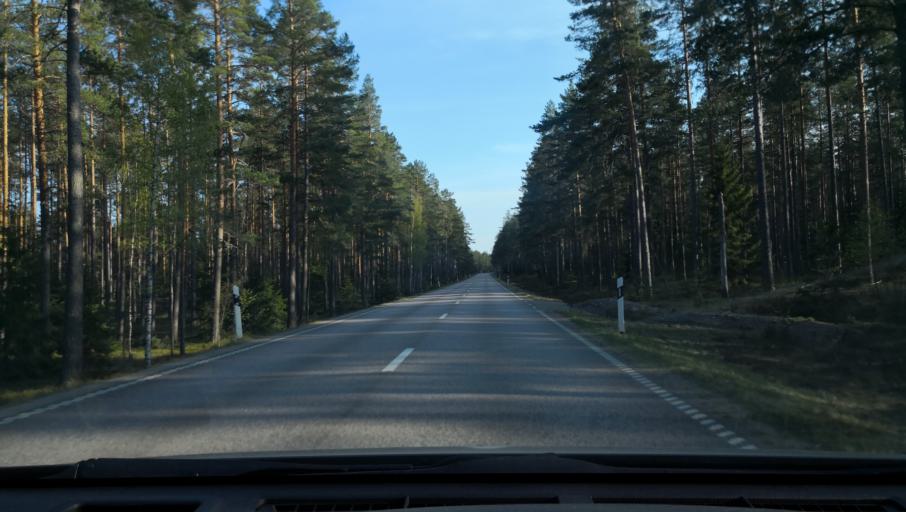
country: SE
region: Uppsala
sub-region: Heby Kommun
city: Tarnsjo
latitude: 60.1144
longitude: 16.8854
